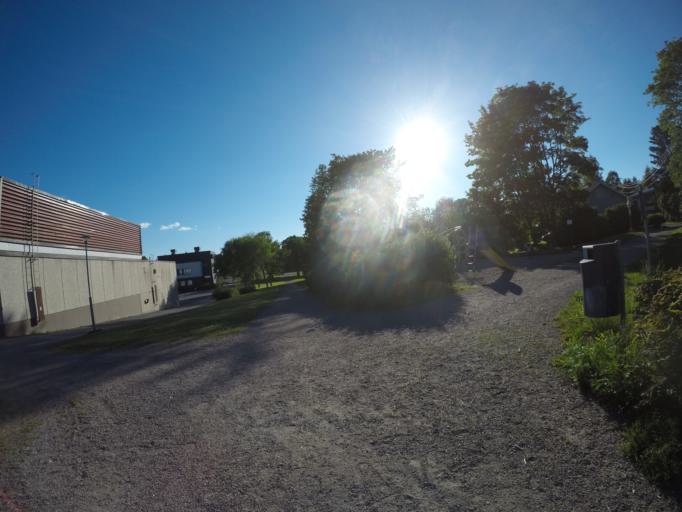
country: FI
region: Haeme
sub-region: Haemeenlinna
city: Haemeenlinna
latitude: 60.9884
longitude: 24.4464
